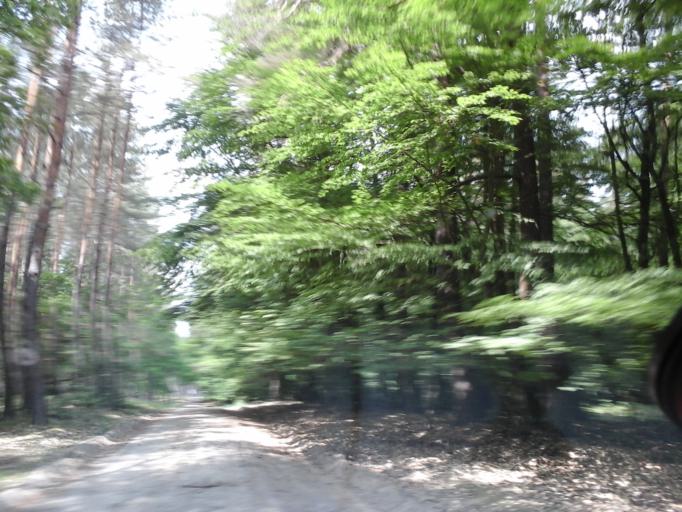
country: PL
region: West Pomeranian Voivodeship
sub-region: Powiat choszczenski
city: Drawno
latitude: 53.1627
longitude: 15.7941
